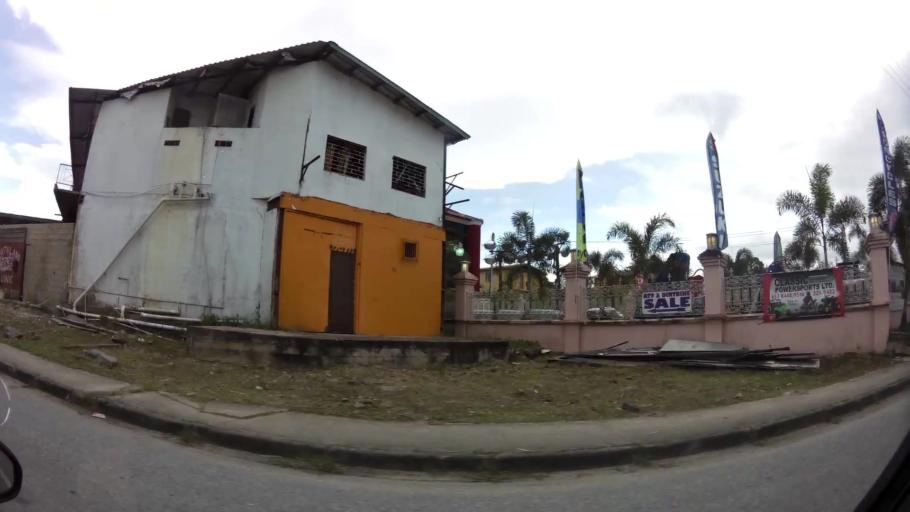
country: TT
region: City of San Fernando
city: Mon Repos
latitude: 10.2595
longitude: -61.4578
